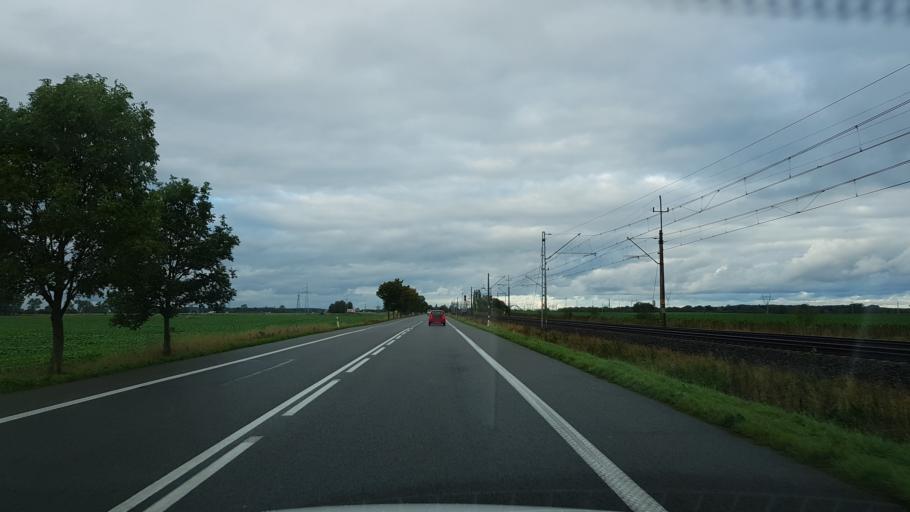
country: PL
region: West Pomeranian Voivodeship
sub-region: Powiat kamienski
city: Wolin
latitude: 53.8461
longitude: 14.6633
